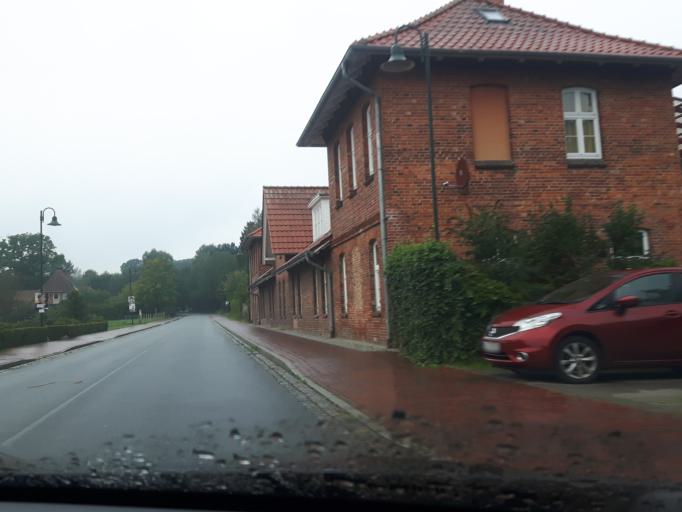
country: DE
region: Lower Saxony
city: Grossenkneten
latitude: 52.9898
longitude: 8.2654
